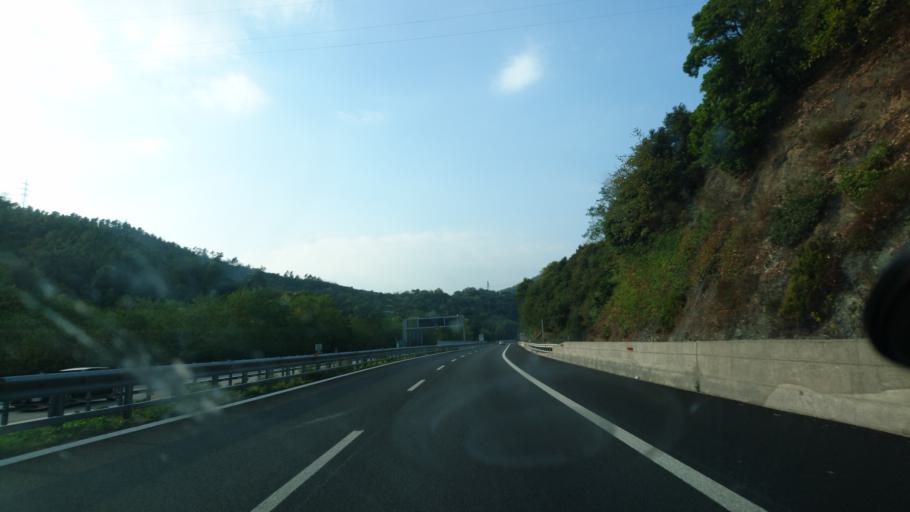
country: IT
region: Liguria
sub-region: Provincia di Savona
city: Valleggia
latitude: 44.2956
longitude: 8.4312
